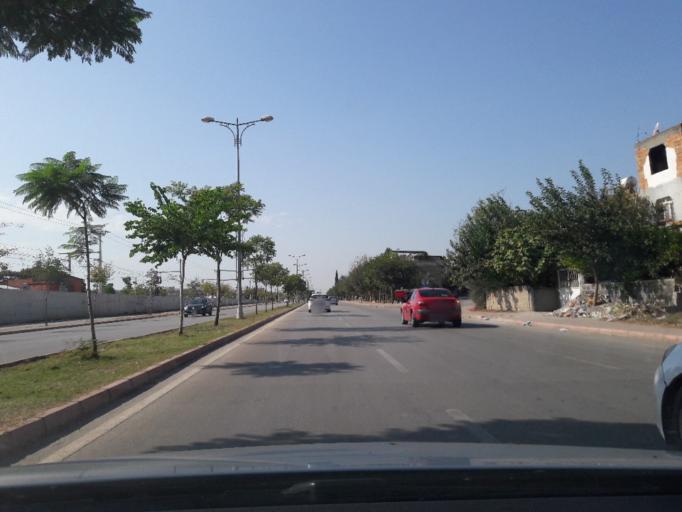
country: TR
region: Adana
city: Seyhan
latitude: 37.0016
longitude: 35.3086
